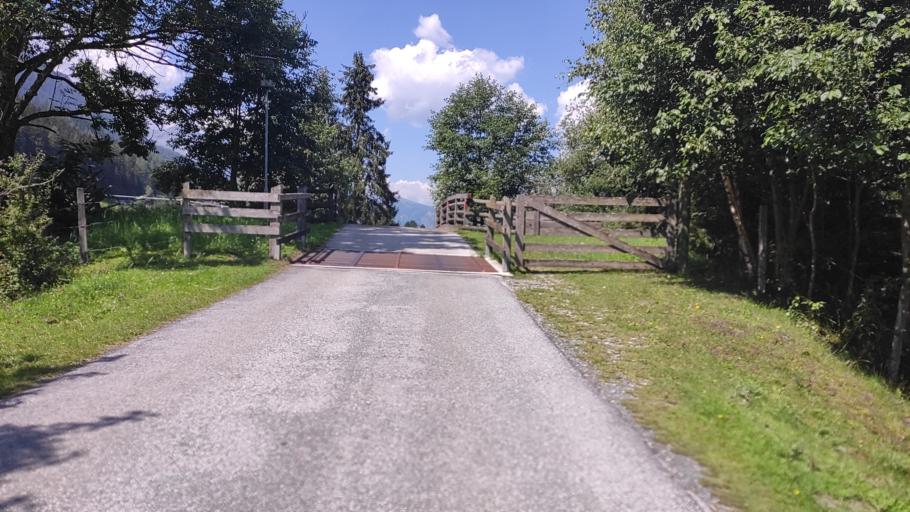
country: AT
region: Salzburg
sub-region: Politischer Bezirk Zell am See
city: Bramberg am Wildkogel
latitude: 47.2528
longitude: 12.3158
